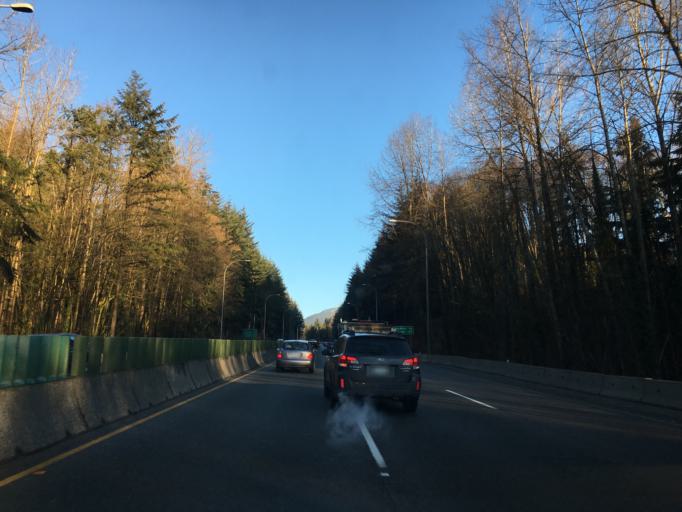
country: CA
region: British Columbia
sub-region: Fraser Valley Regional District
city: North Vancouver
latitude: 49.3192
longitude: -123.0405
